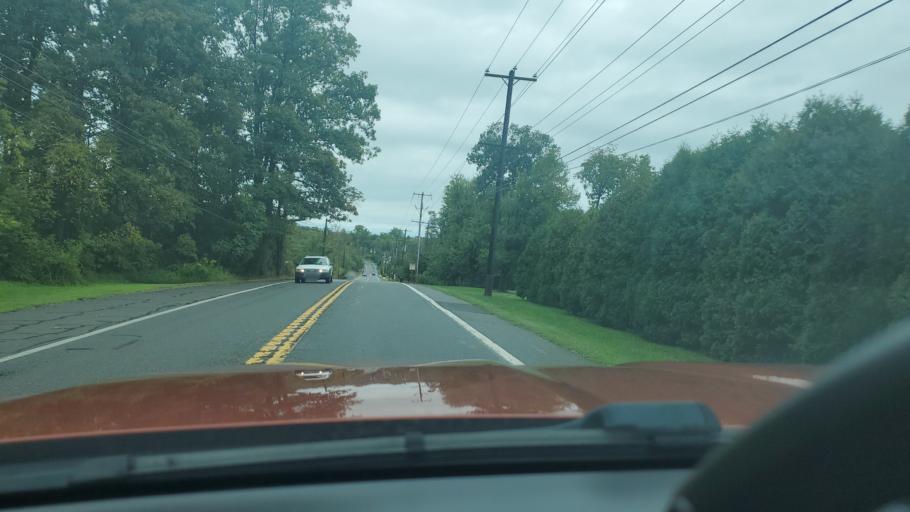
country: US
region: Pennsylvania
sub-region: Montgomery County
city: Spring Mount
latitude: 40.2986
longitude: -75.4803
